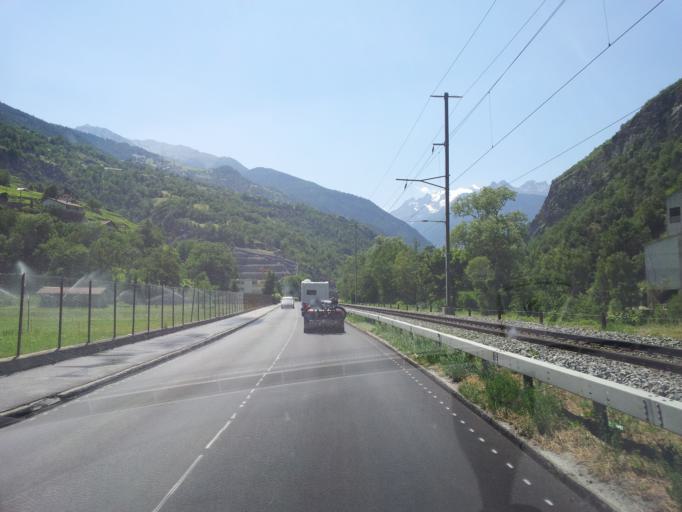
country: CH
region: Valais
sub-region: Visp District
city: Visp
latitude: 46.2837
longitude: 7.8809
